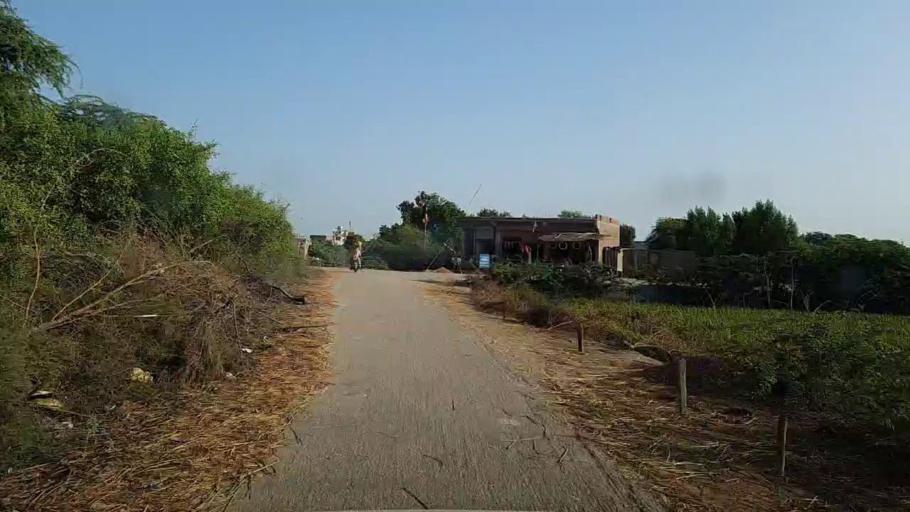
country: PK
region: Sindh
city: Bulri
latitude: 24.7557
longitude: 68.4131
